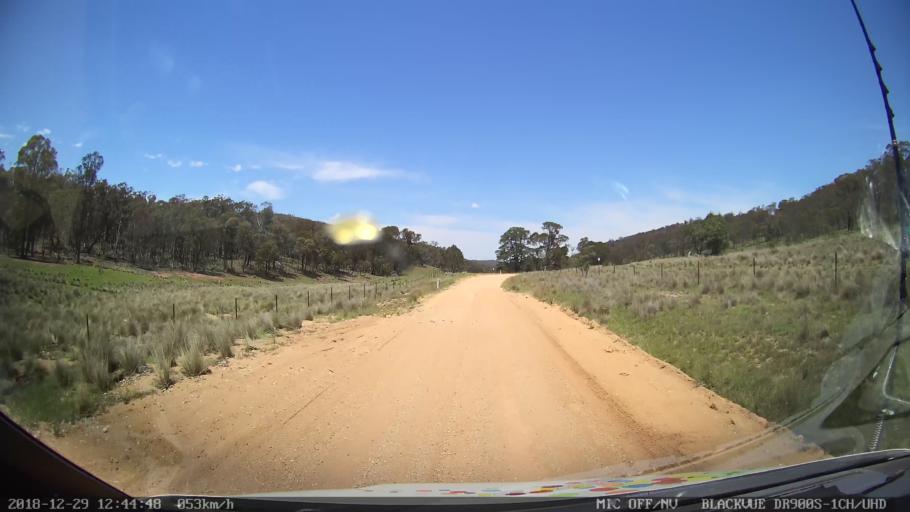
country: AU
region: Australian Capital Territory
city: Macarthur
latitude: -35.6303
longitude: 149.2157
